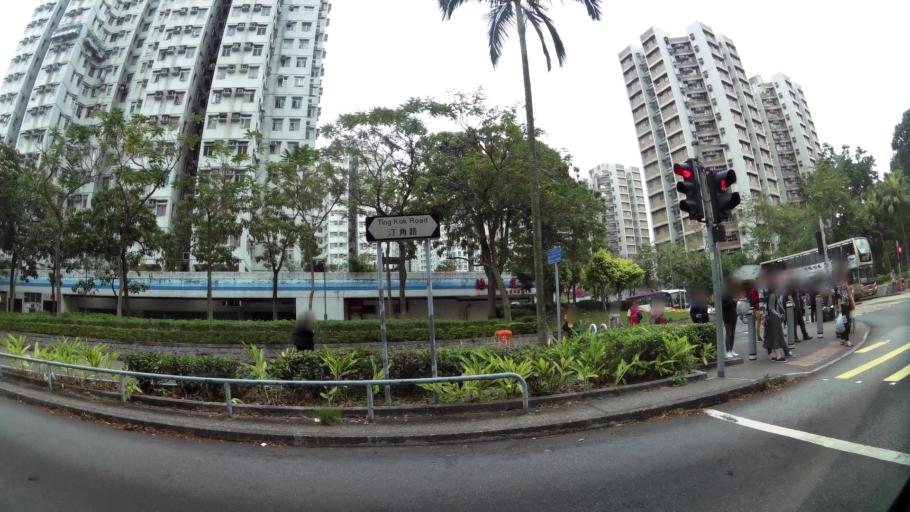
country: HK
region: Tai Po
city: Tai Po
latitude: 22.4532
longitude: 114.1658
